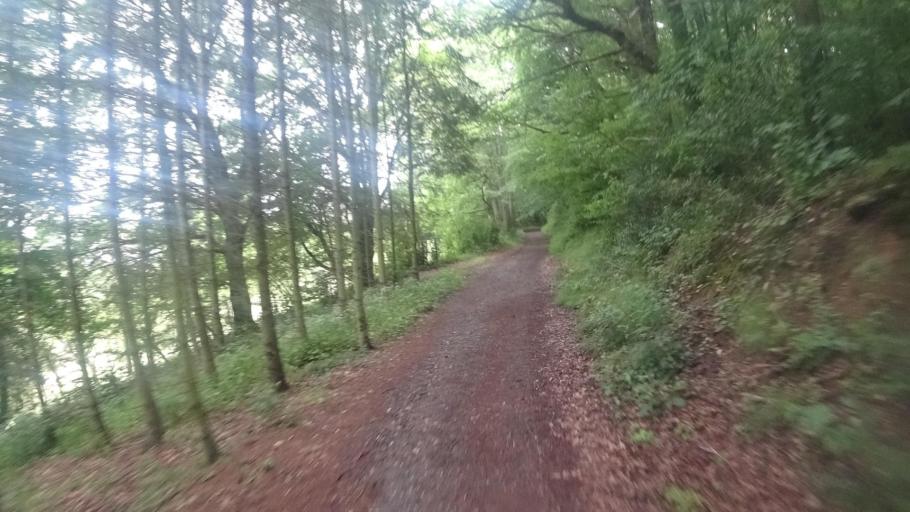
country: DE
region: Rheinland-Pfalz
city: Dernau
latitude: 50.5541
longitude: 7.0512
